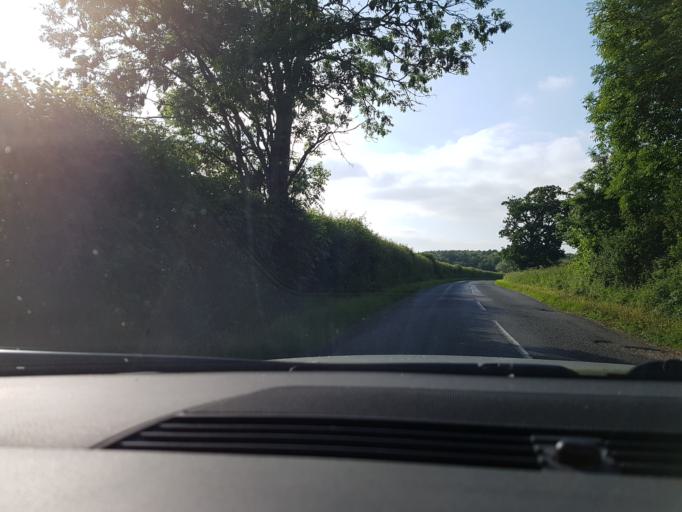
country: GB
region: England
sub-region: Northamptonshire
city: Deanshanger
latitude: 52.0302
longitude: -0.9074
